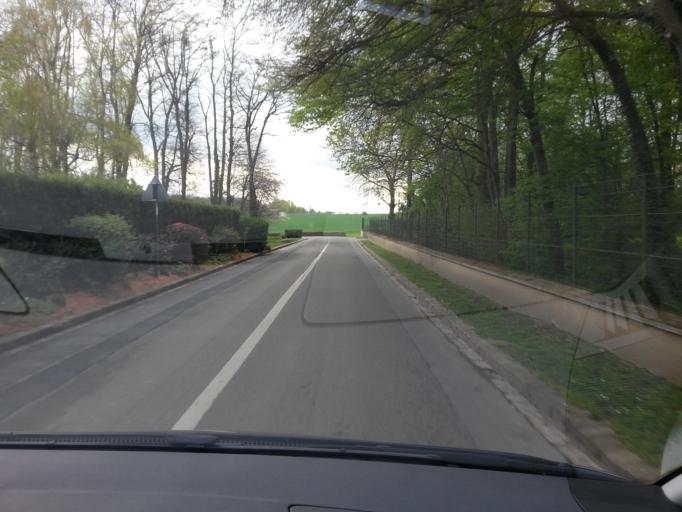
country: FR
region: Picardie
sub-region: Departement de l'Oise
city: Longueil-Sainte-Marie
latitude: 49.3696
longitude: 2.7010
